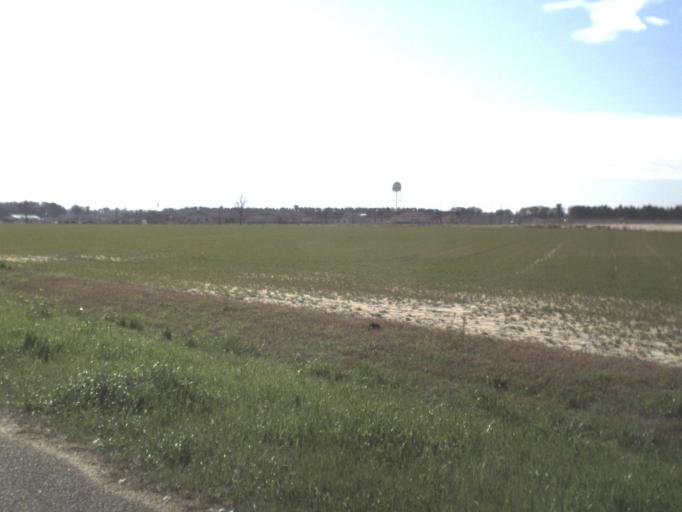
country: US
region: Florida
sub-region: Jackson County
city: Malone
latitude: 30.9760
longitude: -85.1706
